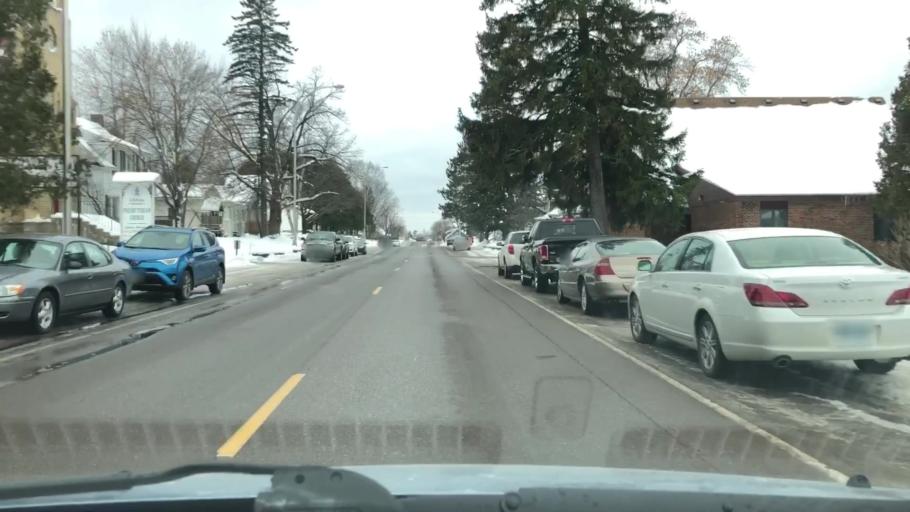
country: US
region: Minnesota
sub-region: Carlton County
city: Carlton
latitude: 46.6640
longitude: -92.4194
